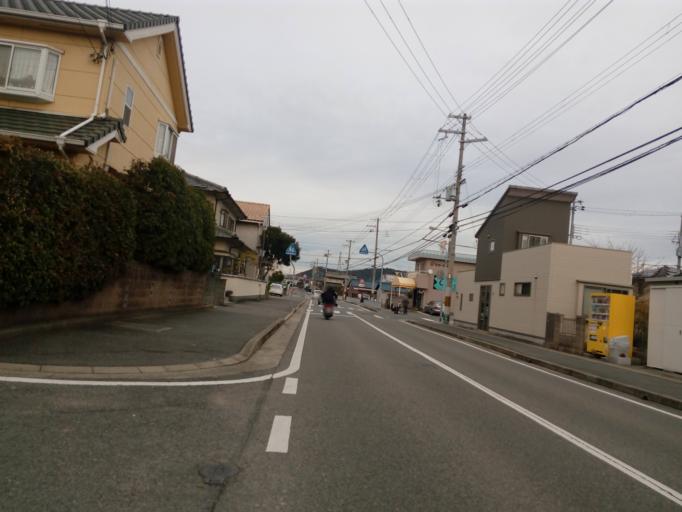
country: JP
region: Hyogo
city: Tatsunocho-tominaga
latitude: 34.7957
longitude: 134.6073
